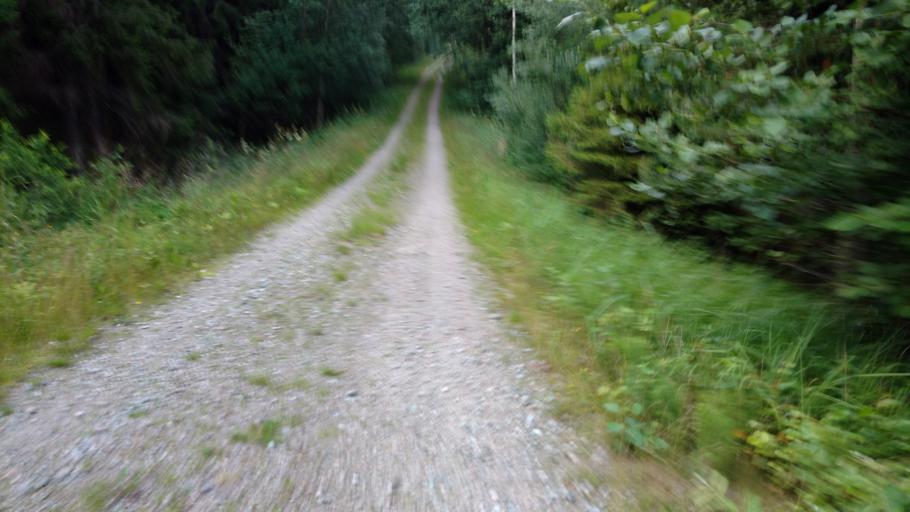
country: FI
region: Varsinais-Suomi
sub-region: Salo
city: Pertteli
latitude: 60.3938
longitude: 23.2273
